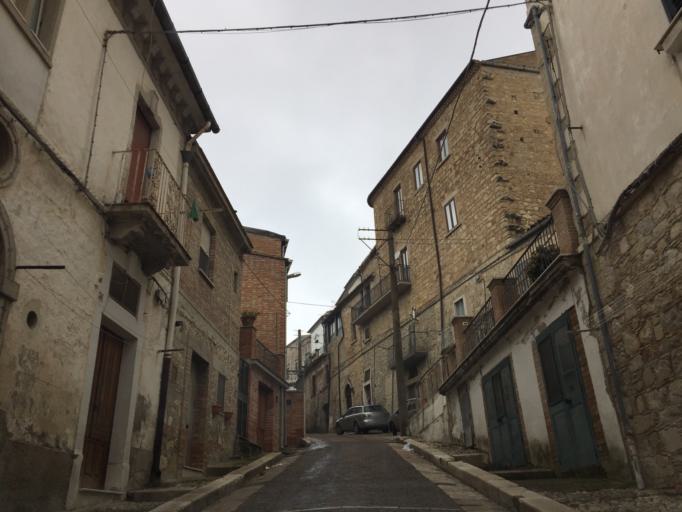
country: IT
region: Apulia
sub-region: Provincia di Foggia
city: Bovino
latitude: 41.2502
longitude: 15.3416
